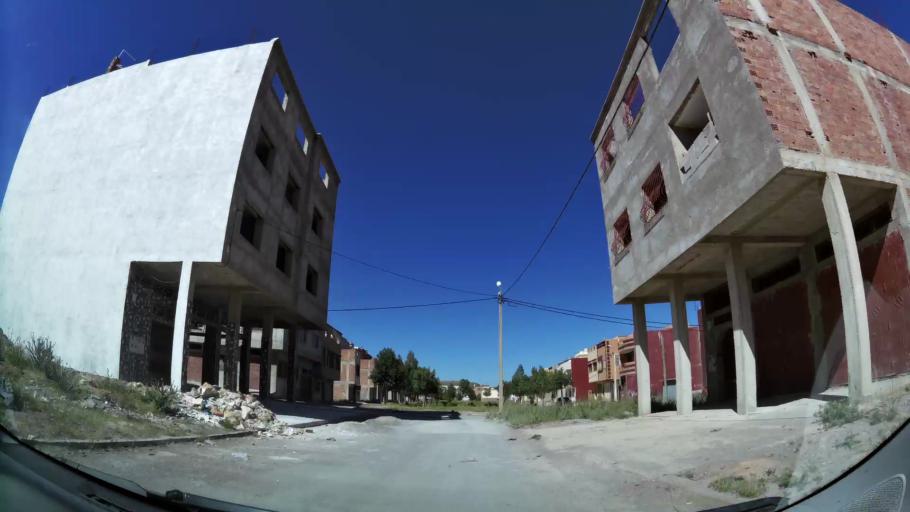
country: MA
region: Oriental
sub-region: Oujda-Angad
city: Oujda
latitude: 34.6509
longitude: -1.8834
